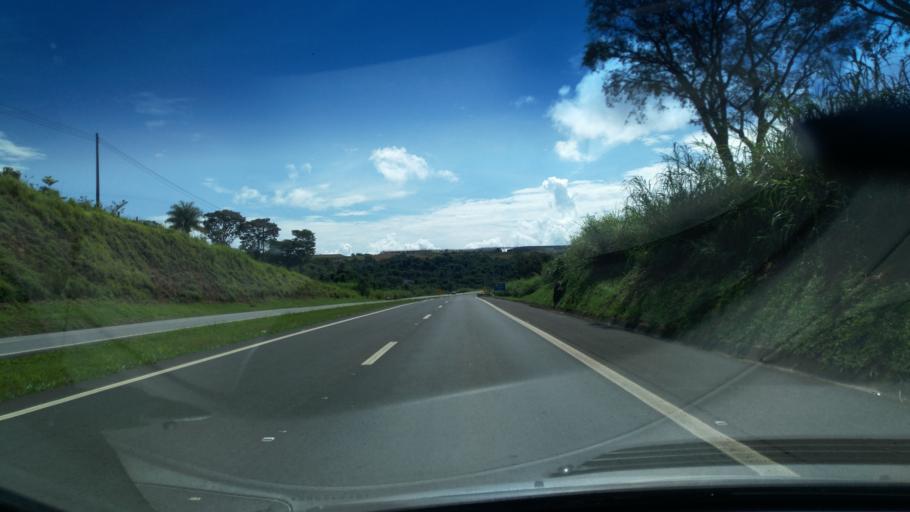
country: BR
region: Sao Paulo
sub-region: Santo Antonio Do Jardim
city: Espirito Santo do Pinhal
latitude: -22.2150
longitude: -46.7854
